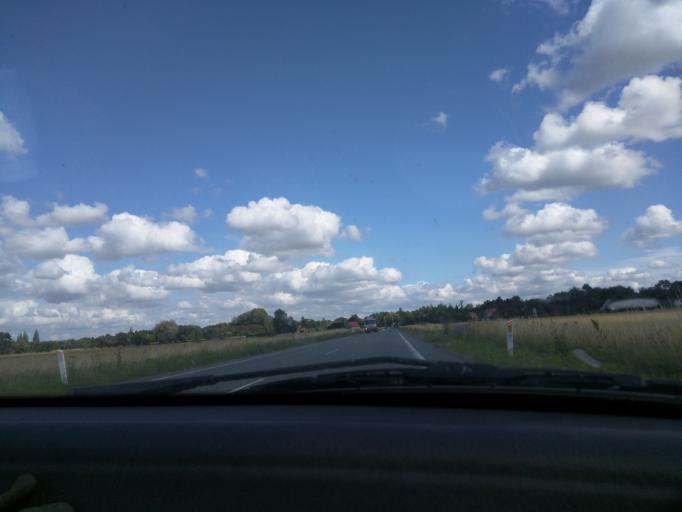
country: DK
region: Zealand
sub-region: Kalundborg Kommune
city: Svebolle
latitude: 55.6637
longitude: 11.2630
